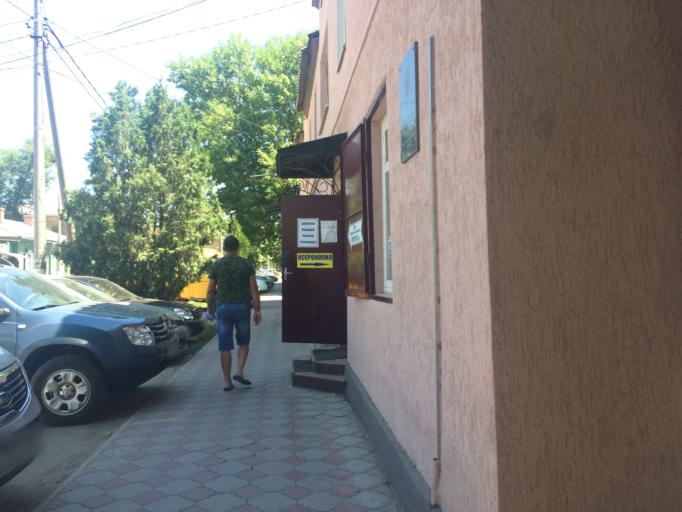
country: RU
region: Rostov
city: Sal'sk
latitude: 46.4737
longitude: 41.5380
